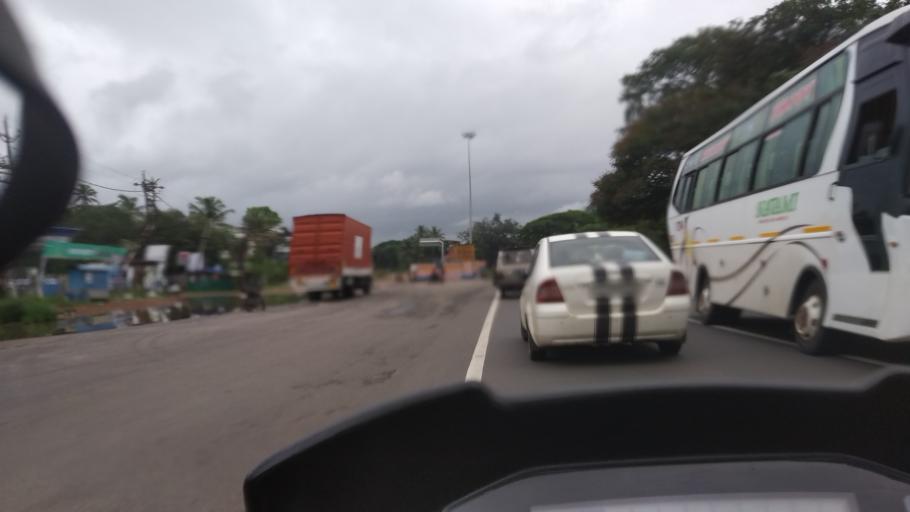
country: IN
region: Kerala
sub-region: Alappuzha
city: Alleppey
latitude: 9.4665
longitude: 76.3390
